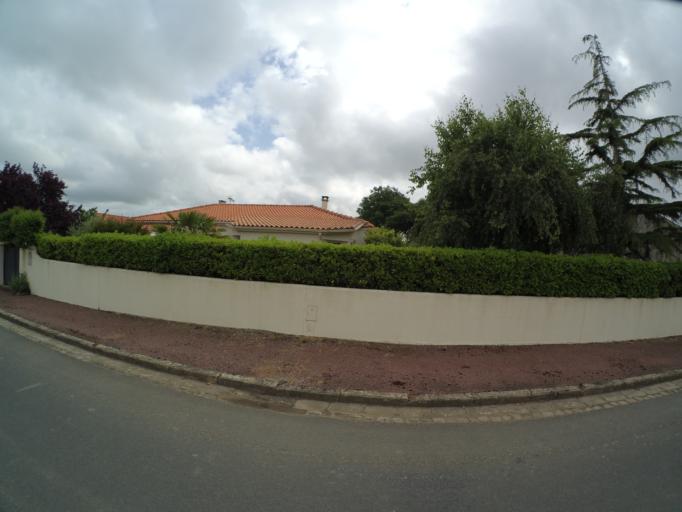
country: FR
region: Poitou-Charentes
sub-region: Departement de la Charente-Maritime
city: Yves
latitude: 46.0197
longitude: -1.0478
